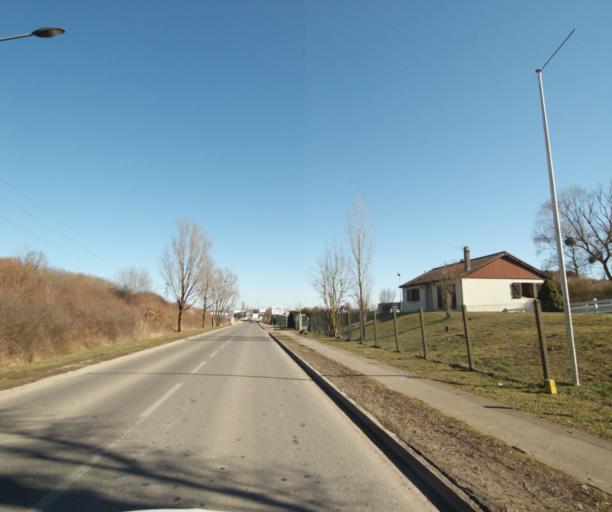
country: FR
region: Lorraine
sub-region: Departement de Meurthe-et-Moselle
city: Fleville-devant-Nancy
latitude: 48.6126
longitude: 6.1980
